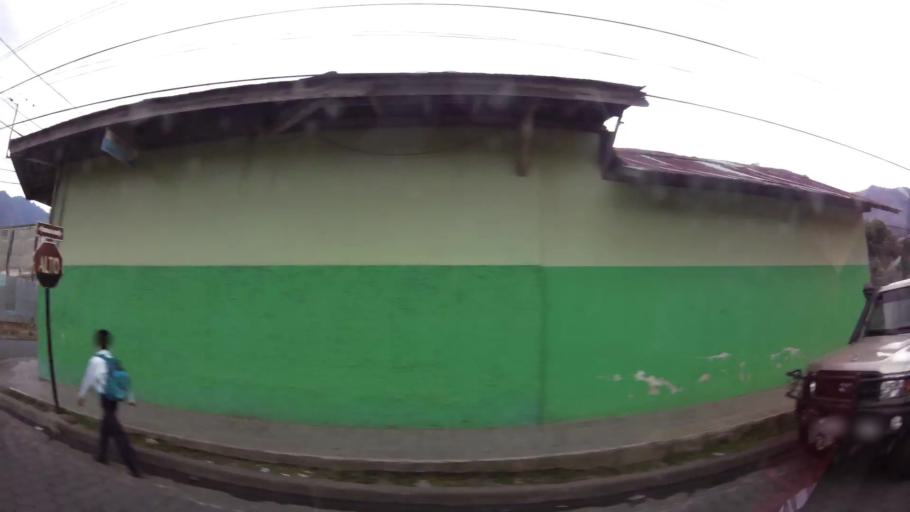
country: NI
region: Jinotega
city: Jinotega
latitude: 13.0870
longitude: -86.0012
